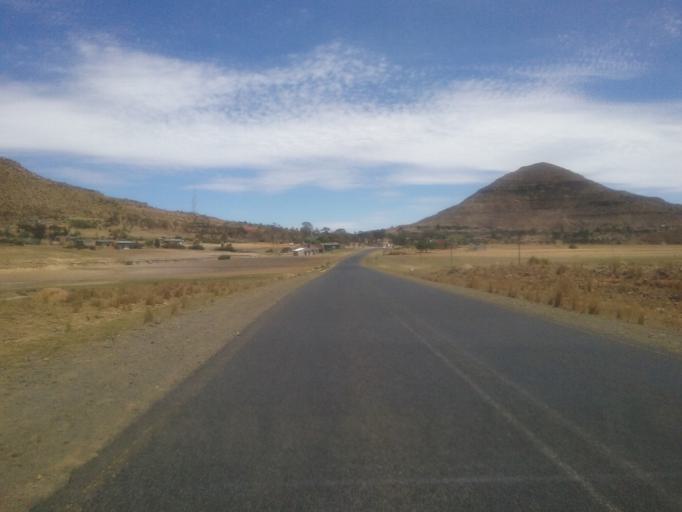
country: LS
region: Mafeteng
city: Mafeteng
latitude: -29.9600
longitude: 27.2925
